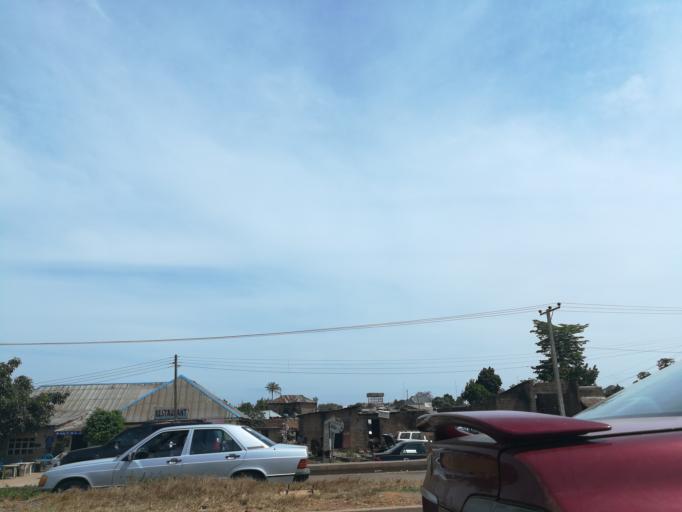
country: NG
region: Plateau
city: Bukuru
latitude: 9.8016
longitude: 8.8599
